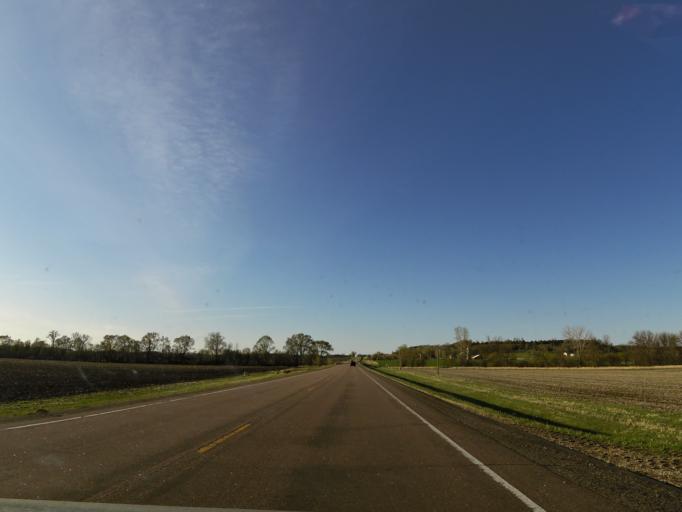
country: US
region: Minnesota
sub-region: Goodhue County
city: Cannon Falls
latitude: 44.5588
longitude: -92.9949
